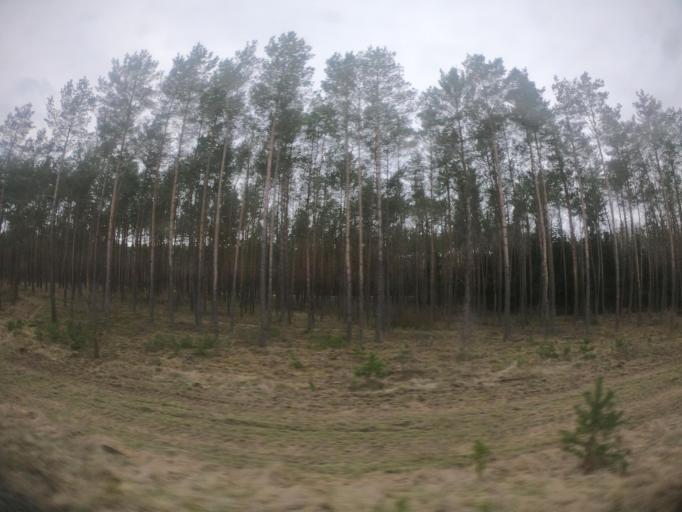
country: PL
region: Pomeranian Voivodeship
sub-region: Powiat czluchowski
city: Czarne
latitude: 53.7455
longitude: 16.8461
